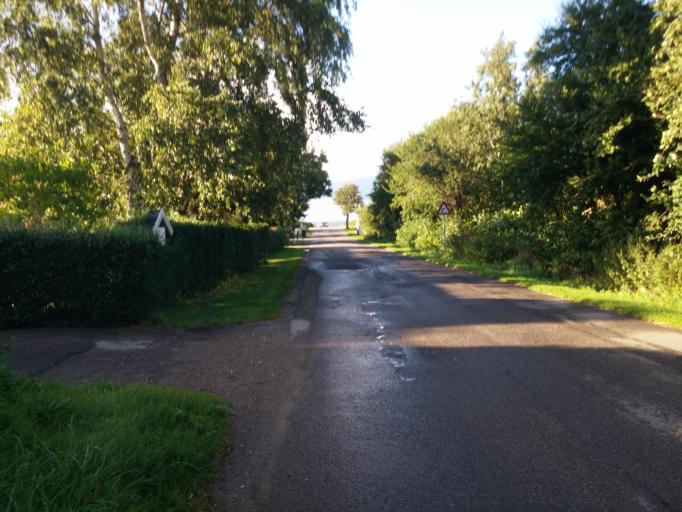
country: DK
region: Zealand
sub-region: Kalundborg Kommune
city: Svebolle
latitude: 55.7525
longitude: 11.3385
